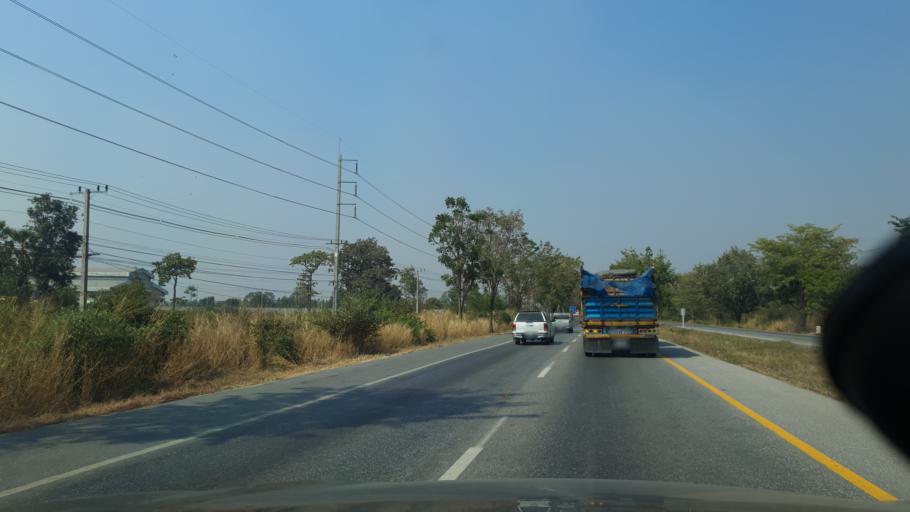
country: TH
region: Kamphaeng Phet
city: Khanu Woralaksaburi
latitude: 16.0594
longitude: 99.7411
